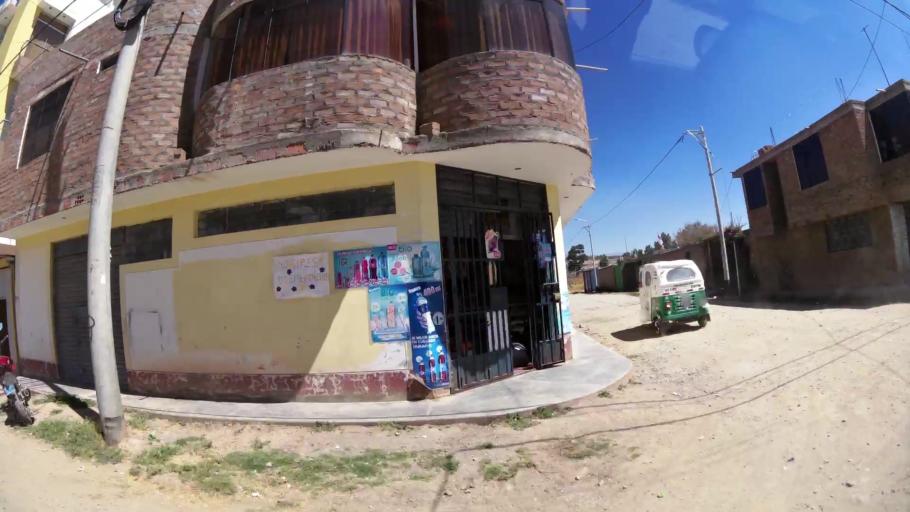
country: PE
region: Junin
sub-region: Provincia de Jauja
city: Jauja
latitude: -11.7752
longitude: -75.4911
